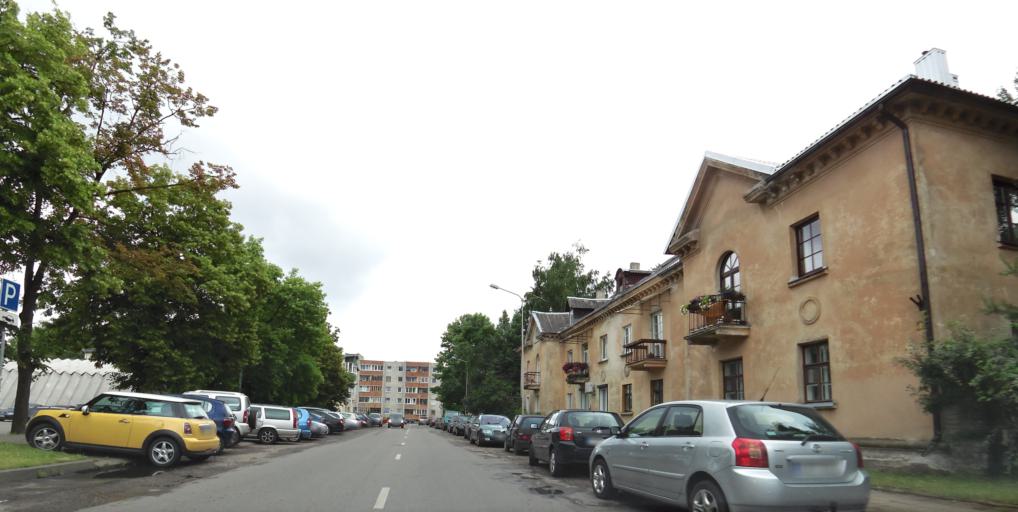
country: LT
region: Vilnius County
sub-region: Vilnius
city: Vilnius
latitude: 54.7097
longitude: 25.2879
